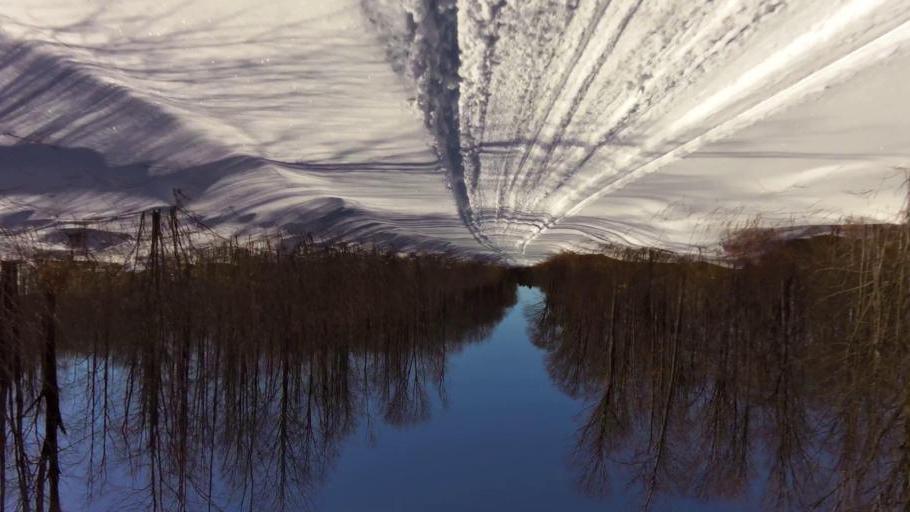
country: US
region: New York
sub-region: Cattaraugus County
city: Franklinville
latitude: 42.3459
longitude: -78.3430
